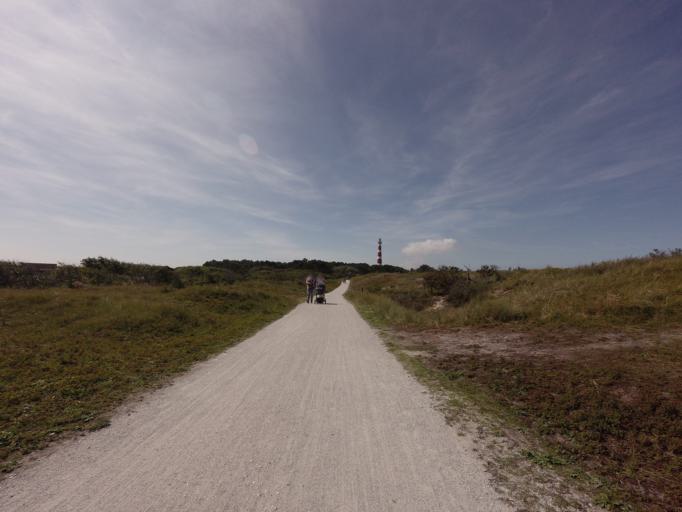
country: NL
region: Friesland
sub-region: Gemeente Ameland
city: Hollum
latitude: 53.4505
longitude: 5.6320
